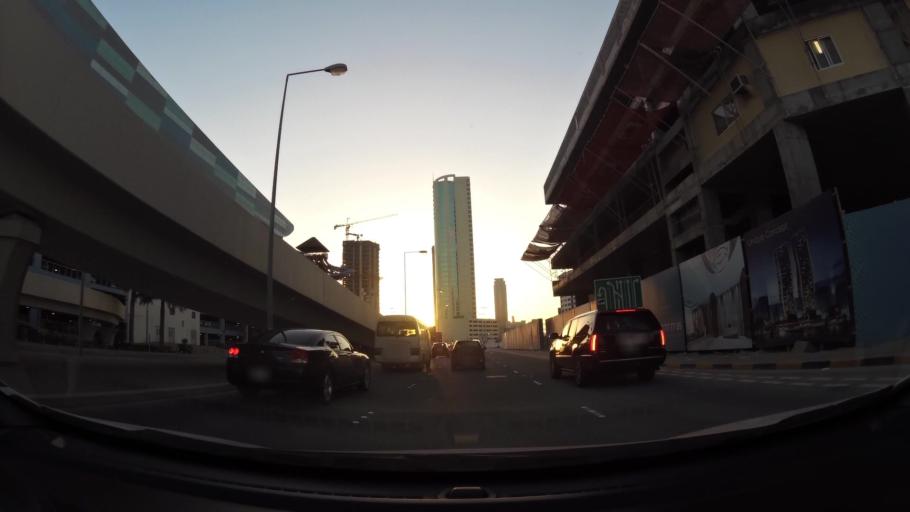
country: BH
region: Manama
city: Jidd Hafs
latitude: 26.2351
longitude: 50.5532
